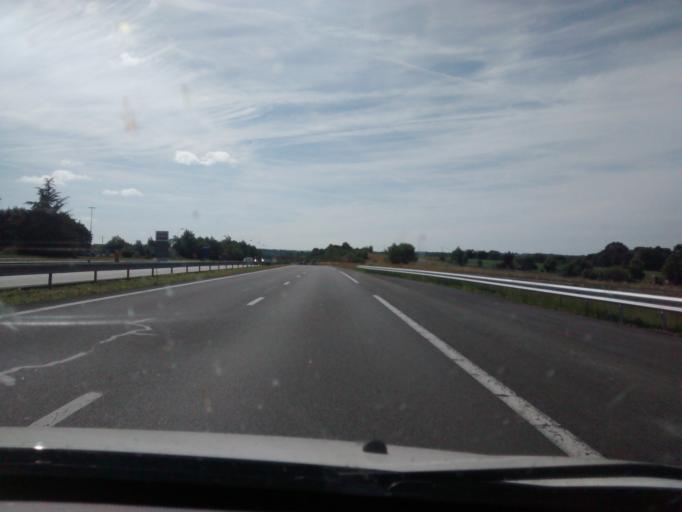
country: FR
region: Pays de la Loire
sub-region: Departement de la Mayenne
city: Bonchamp-les-Laval
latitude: 48.0967
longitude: -0.6966
